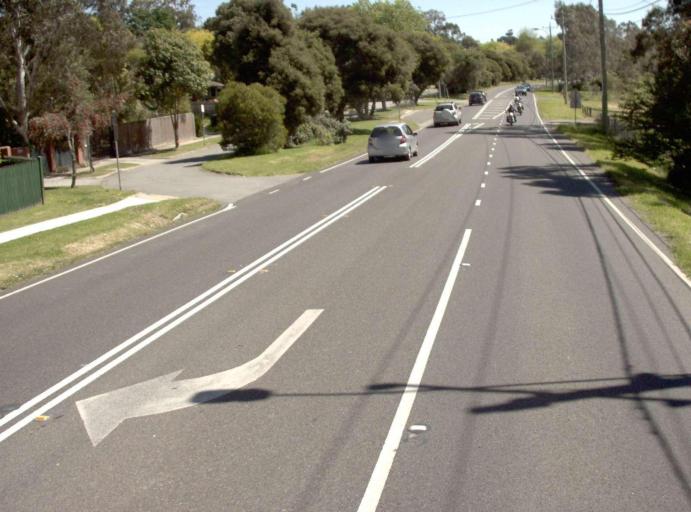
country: AU
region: Victoria
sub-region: Banyule
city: Darch
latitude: -37.7559
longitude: 145.1055
